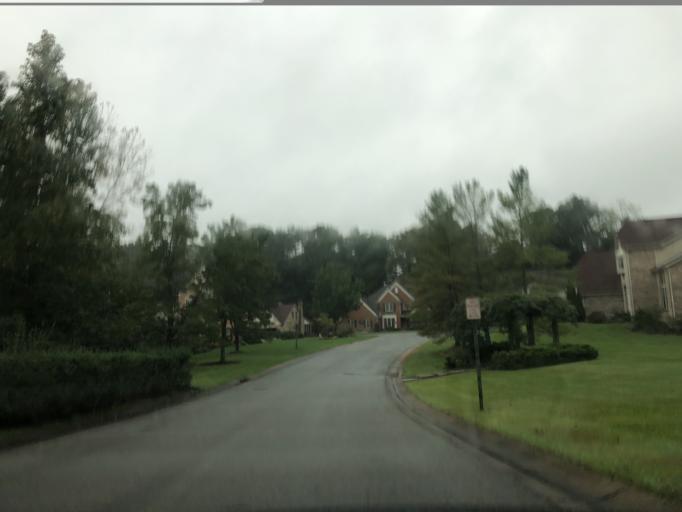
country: US
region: Ohio
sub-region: Hamilton County
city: The Village of Indian Hill
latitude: 39.2662
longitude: -84.2859
